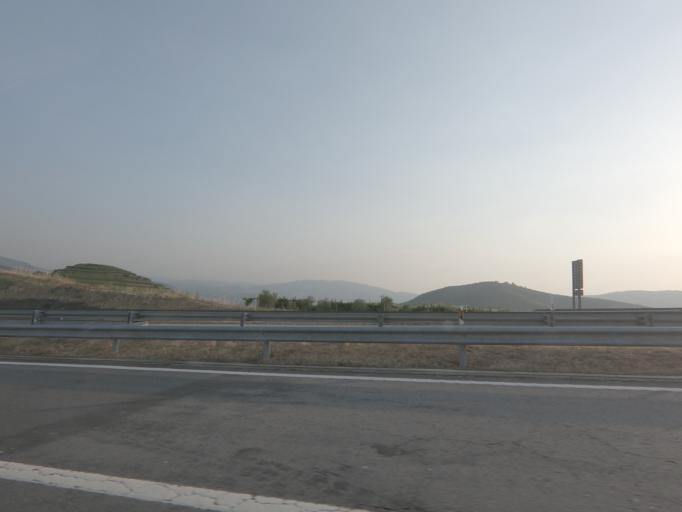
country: PT
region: Vila Real
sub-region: Peso da Regua
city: Peso da Regua
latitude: 41.1905
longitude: -7.7495
